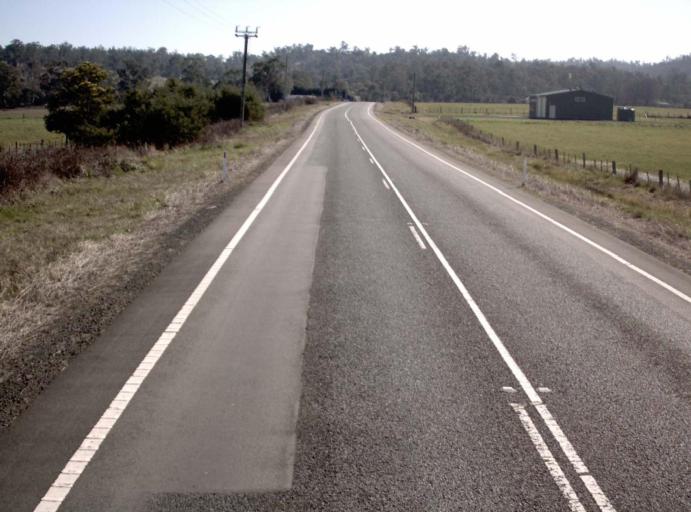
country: AU
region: Tasmania
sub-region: Launceston
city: Mayfield
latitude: -41.3144
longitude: 147.0535
